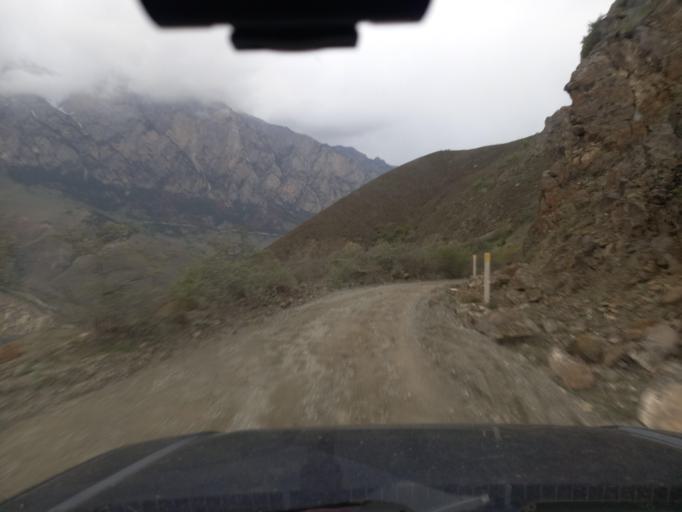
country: RU
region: North Ossetia
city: Mizur
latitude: 42.8524
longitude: 44.1617
